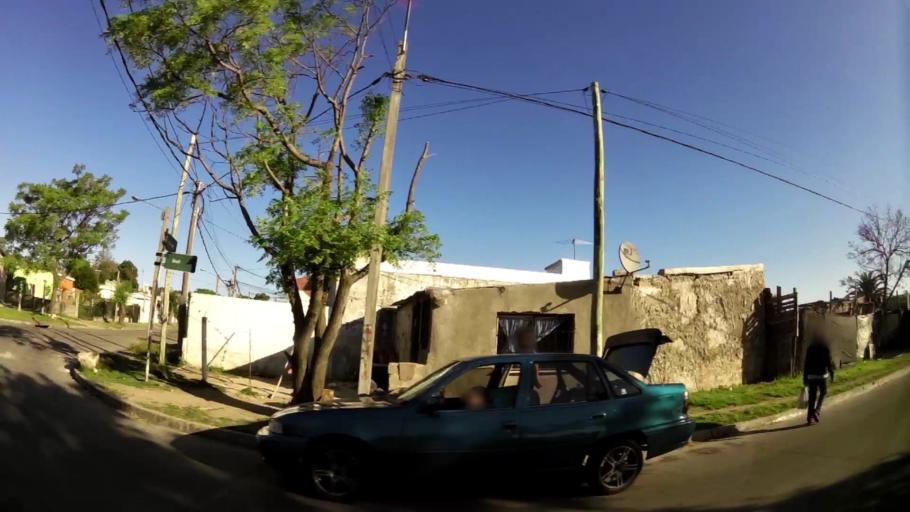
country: UY
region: Montevideo
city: Montevideo
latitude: -34.8399
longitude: -56.2149
